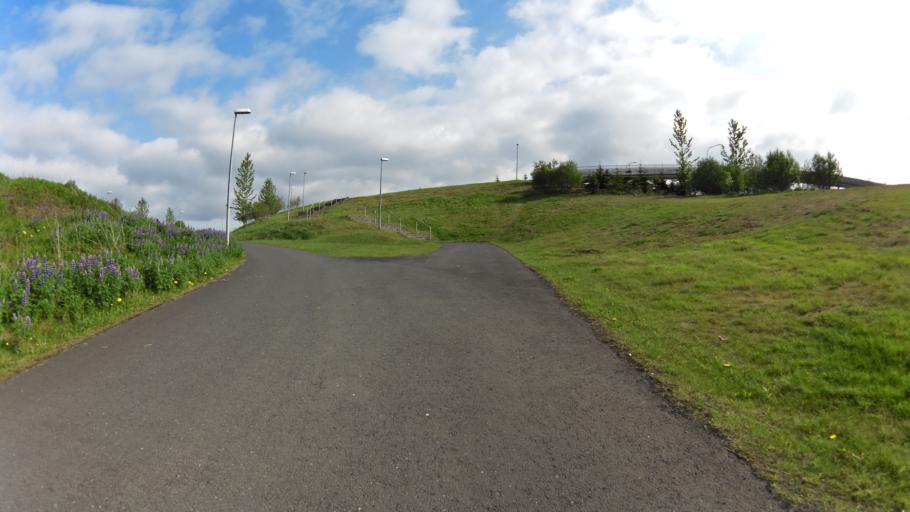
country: IS
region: Capital Region
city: Reykjavik
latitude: 64.1160
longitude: -21.8426
